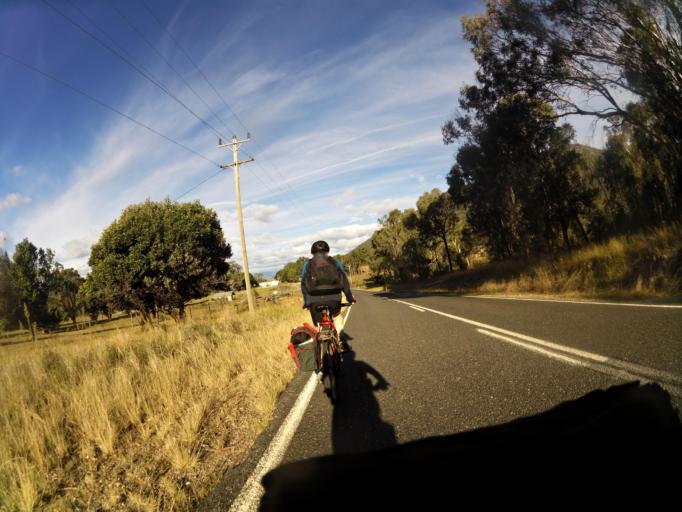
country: AU
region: New South Wales
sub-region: Greater Hume Shire
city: Holbrook
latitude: -35.9870
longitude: 147.8314
